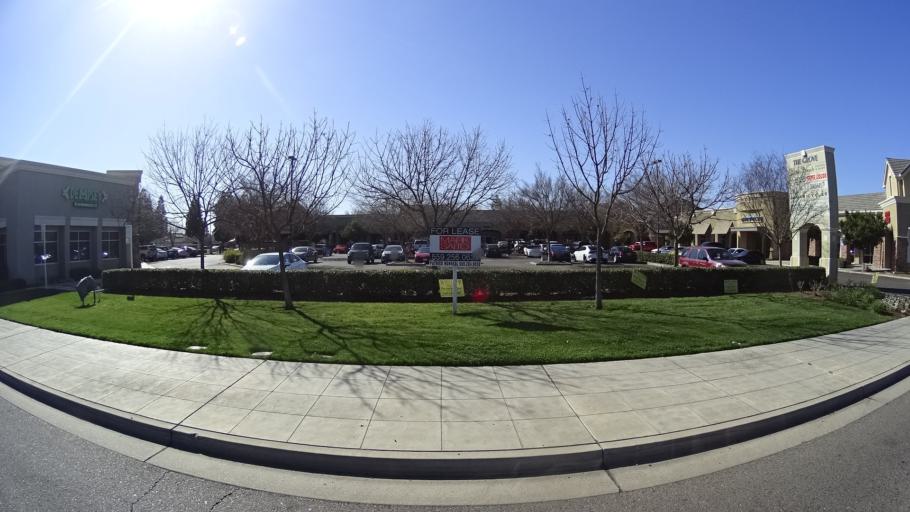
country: US
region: California
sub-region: Fresno County
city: West Park
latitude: 36.8299
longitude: -119.8632
